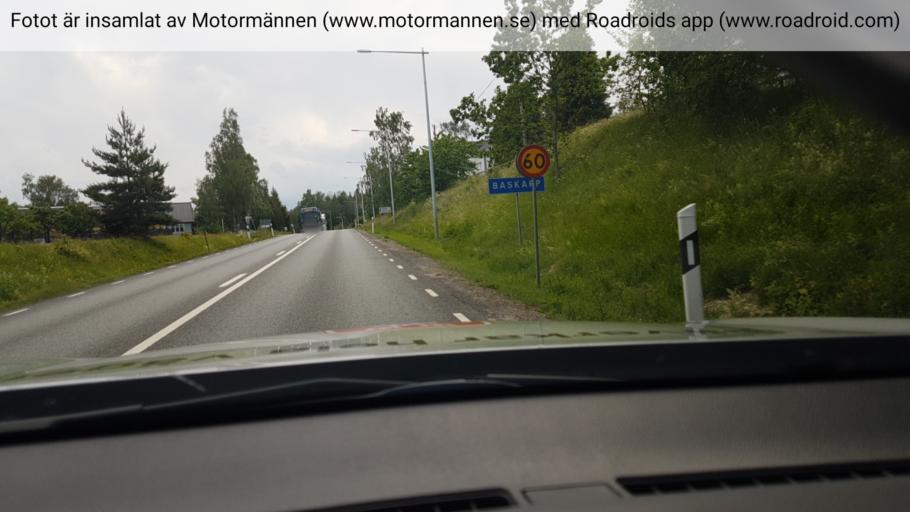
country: SE
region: Joenkoeping
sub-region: Habo Kommun
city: Habo
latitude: 58.0182
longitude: 14.1458
